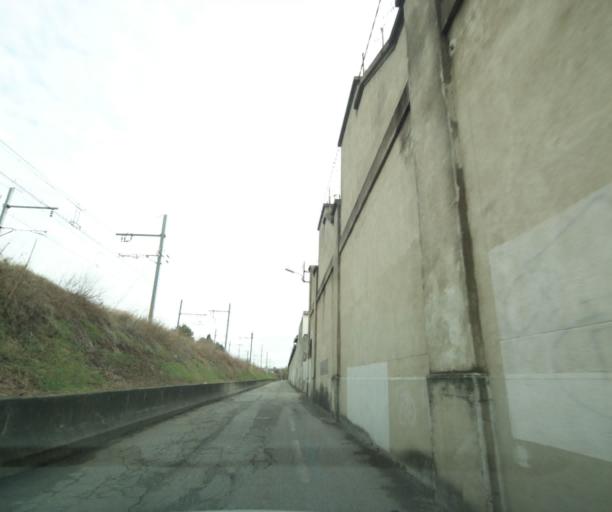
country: FR
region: Rhone-Alpes
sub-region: Departement de la Drome
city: Valence
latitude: 44.9428
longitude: 4.8966
